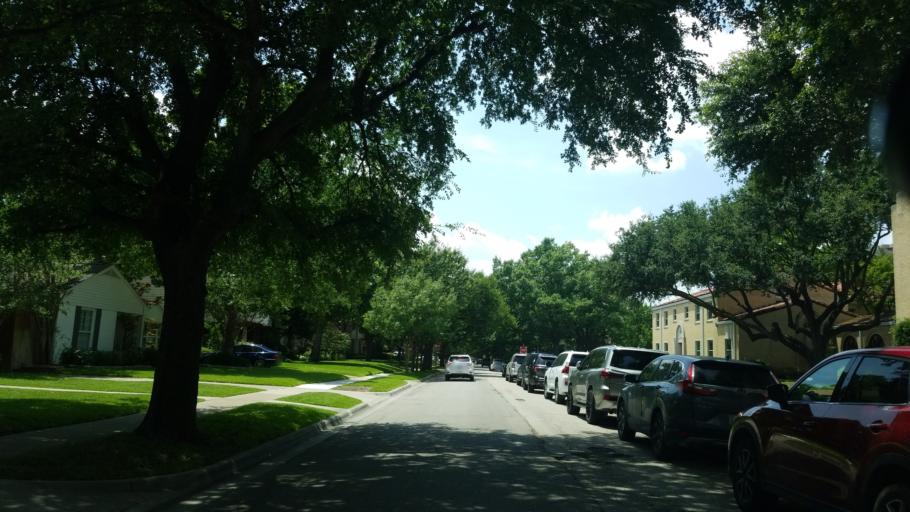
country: US
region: Texas
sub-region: Dallas County
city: University Park
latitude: 32.8599
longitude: -96.8054
